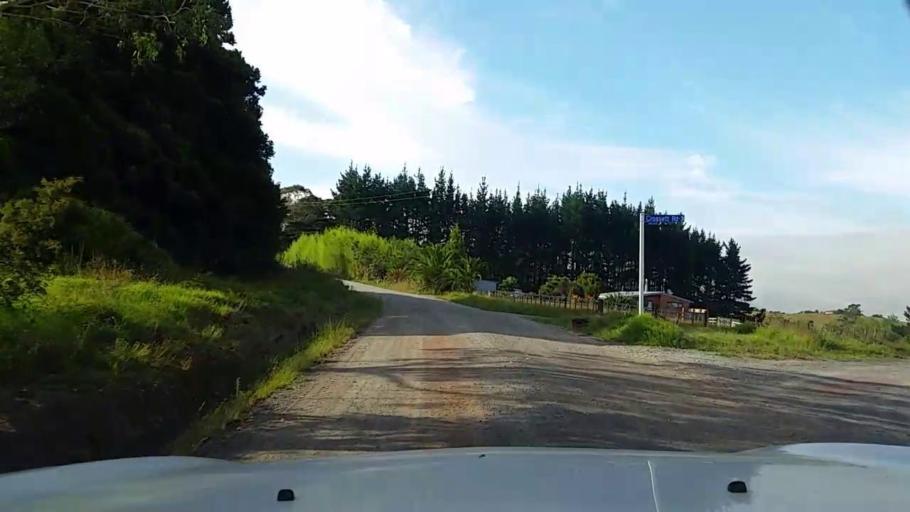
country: NZ
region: Northland
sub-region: Whangarei
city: Maungatapere
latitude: -35.6795
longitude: 174.1784
